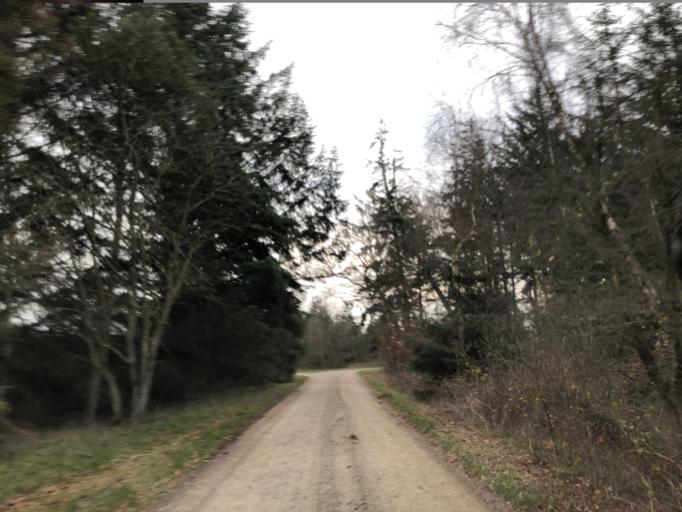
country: DK
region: Central Jutland
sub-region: Holstebro Kommune
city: Ulfborg
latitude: 56.2881
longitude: 8.1856
